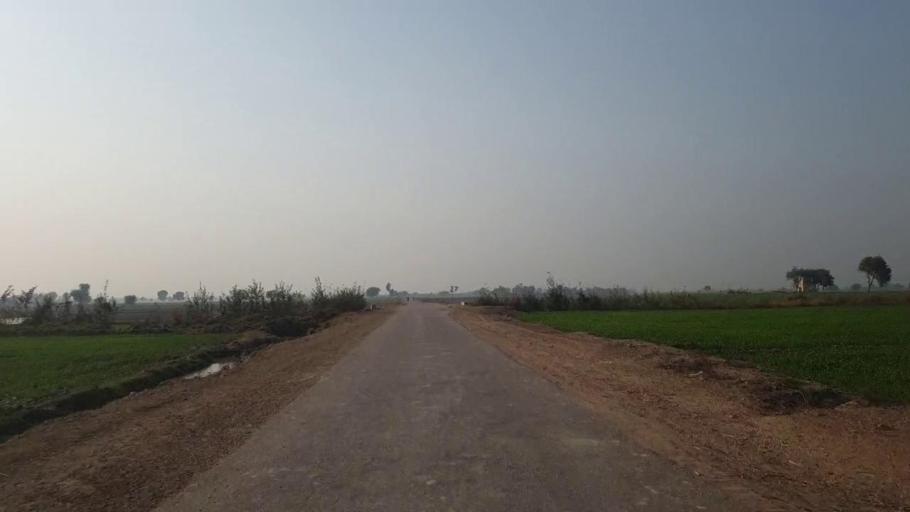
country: PK
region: Sindh
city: Shahdadpur
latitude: 25.9659
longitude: 68.5623
